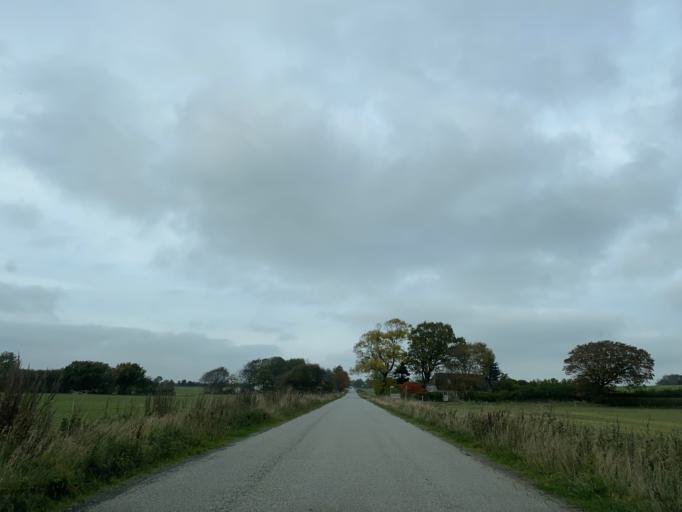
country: DK
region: South Denmark
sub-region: Haderslev Kommune
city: Starup
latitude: 55.1804
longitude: 9.5171
